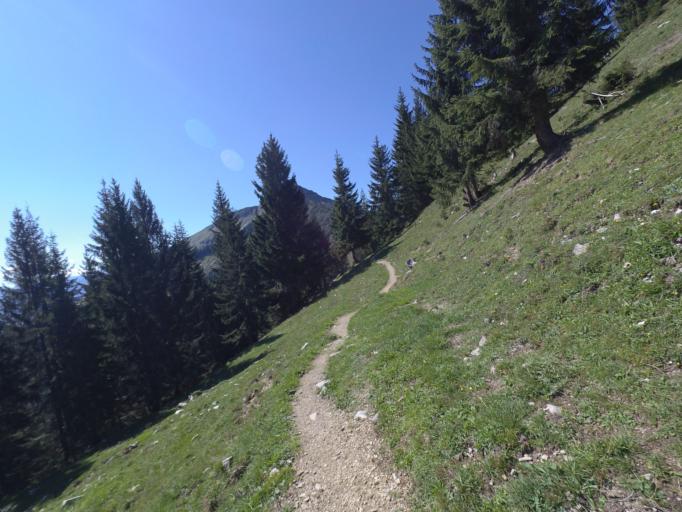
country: AT
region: Salzburg
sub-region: Politischer Bezirk Salzburg-Umgebung
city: Hintersee
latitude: 47.6877
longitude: 13.2607
